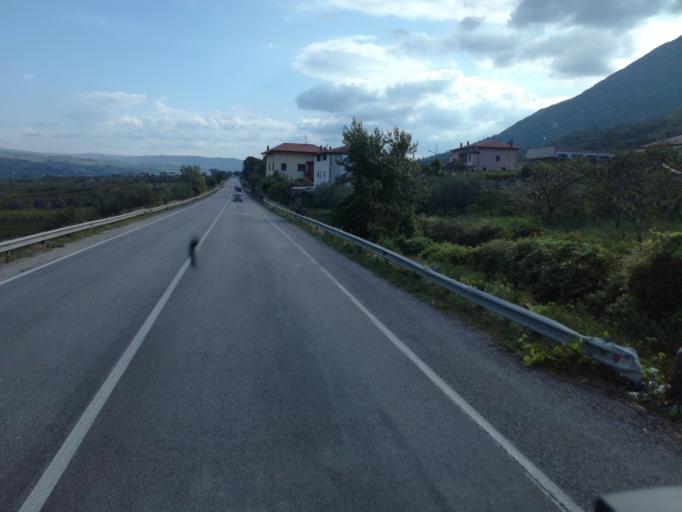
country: IT
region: Campania
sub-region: Provincia di Benevento
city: San Lorenzo Maggiore
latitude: 41.2070
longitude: 14.5988
